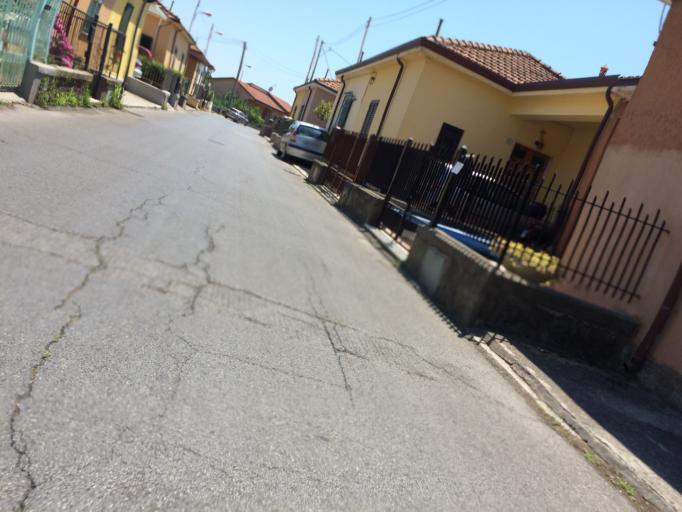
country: IT
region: Tuscany
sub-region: Provincia di Massa-Carrara
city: Massa
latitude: 44.0394
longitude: 10.1279
